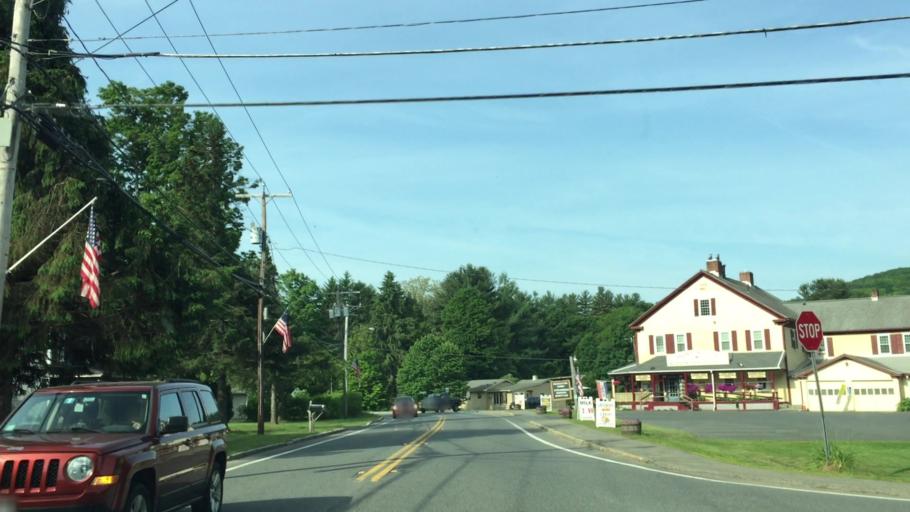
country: US
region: Massachusetts
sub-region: Hampshire County
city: Westhampton
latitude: 42.2487
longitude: -72.8681
